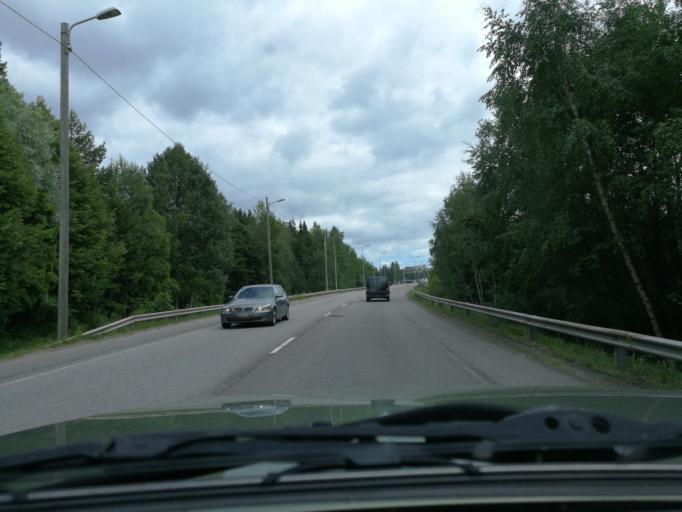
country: FI
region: Uusimaa
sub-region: Helsinki
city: Vantaa
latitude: 60.3117
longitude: 25.0920
